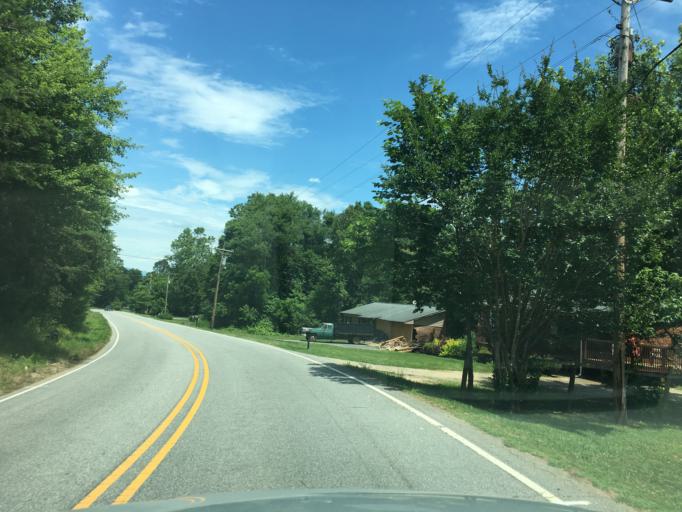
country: US
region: North Carolina
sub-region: Burke County
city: Glen Alpine
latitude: 35.6751
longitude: -81.7678
